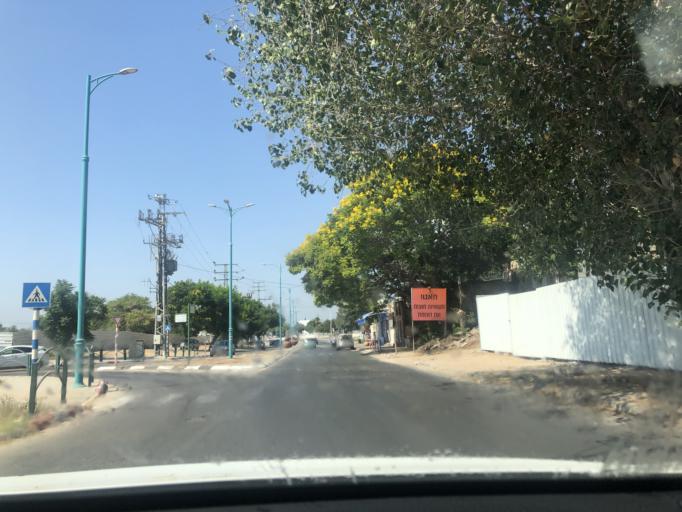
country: IL
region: Central District
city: Lod
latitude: 31.9589
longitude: 34.8982
